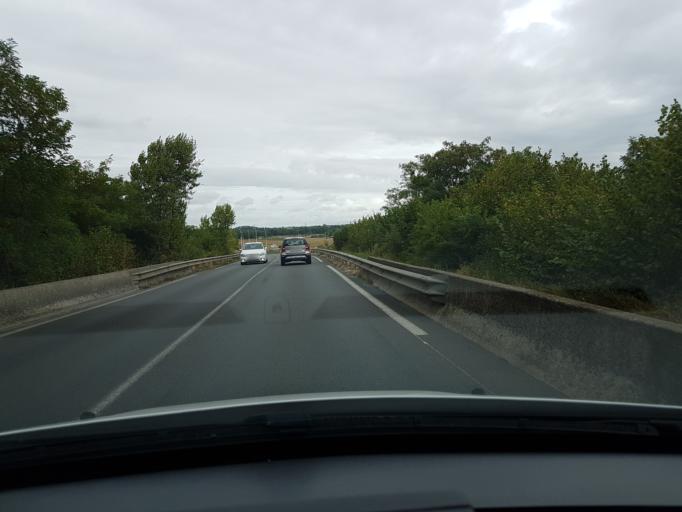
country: FR
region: Centre
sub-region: Departement d'Indre-et-Loire
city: La Ville-aux-Dames
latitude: 47.3909
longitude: 0.7878
